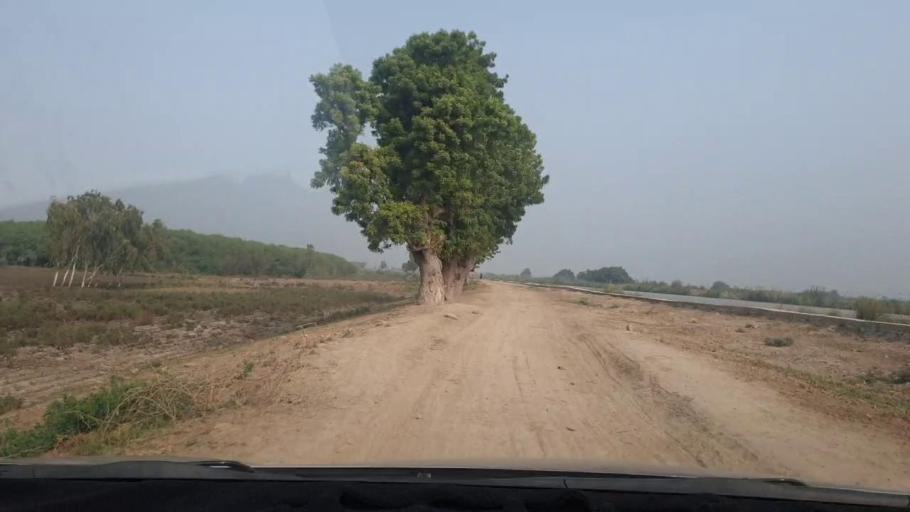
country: PK
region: Sindh
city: Matiari
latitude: 25.6505
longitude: 68.5613
